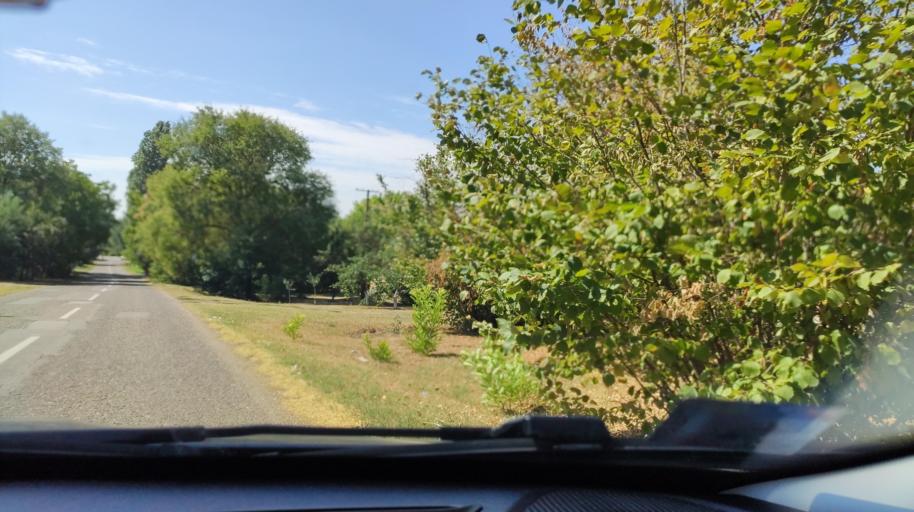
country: RS
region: Autonomna Pokrajina Vojvodina
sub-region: Severnobacki Okrug
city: Backa Topola
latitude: 45.8216
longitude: 19.6224
